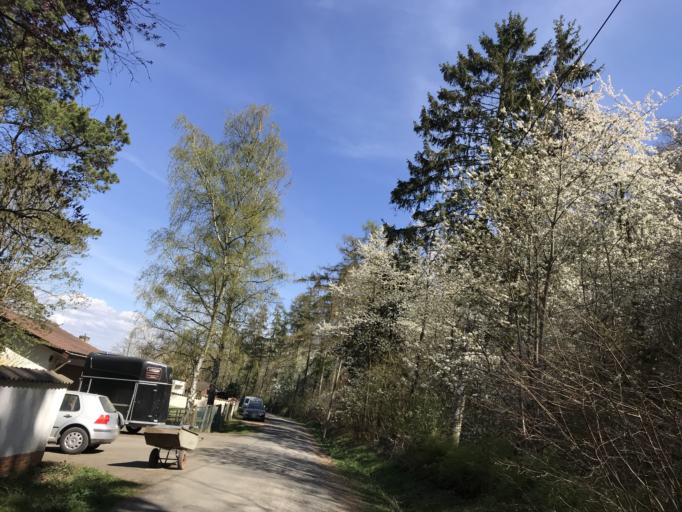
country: DE
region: Hesse
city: Beuern
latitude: 50.6550
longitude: 8.7996
